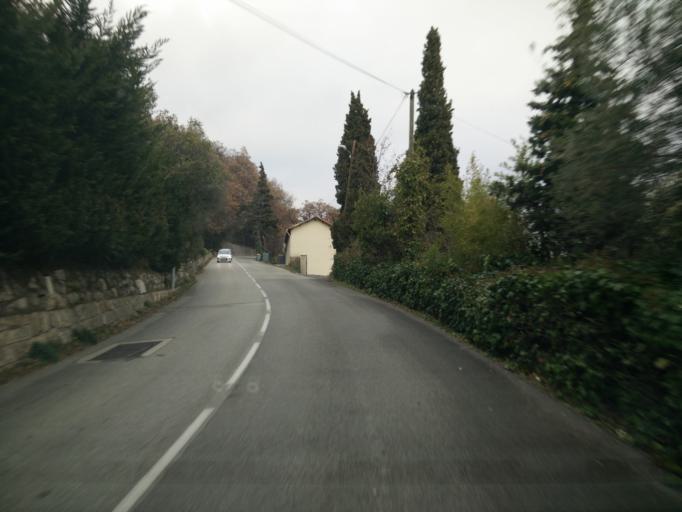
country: FR
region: Provence-Alpes-Cote d'Azur
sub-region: Departement des Alpes-Maritimes
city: Opio
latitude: 43.6826
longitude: 6.9723
